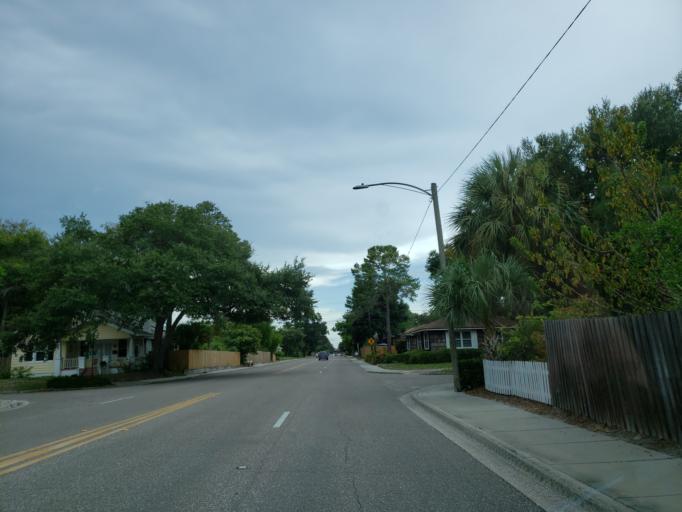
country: US
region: Florida
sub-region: Pinellas County
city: Saint Petersburg
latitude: 27.7759
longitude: -82.6713
